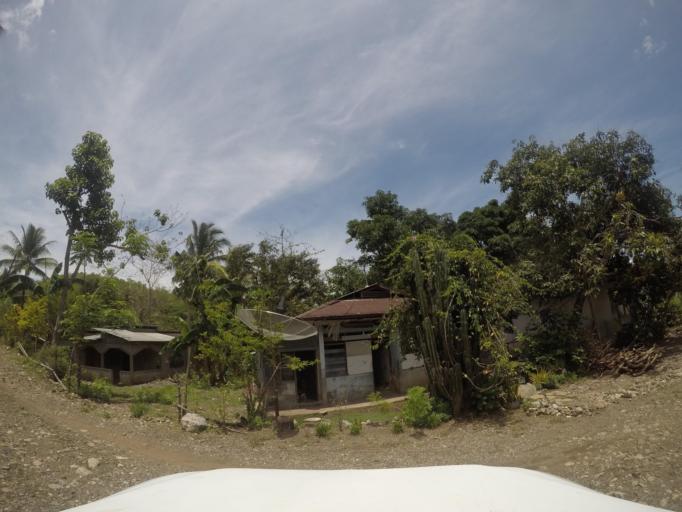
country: TL
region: Bobonaro
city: Maliana
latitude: -9.0000
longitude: 125.2251
